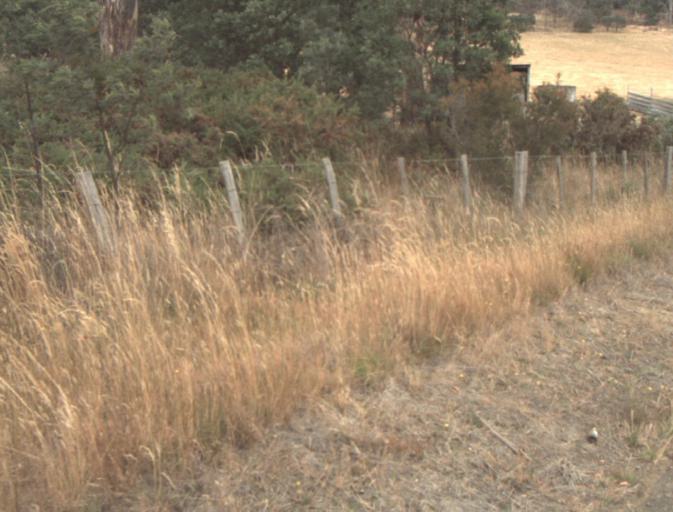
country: AU
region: Tasmania
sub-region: Northern Midlands
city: Evandale
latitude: -41.5217
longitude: 147.3970
